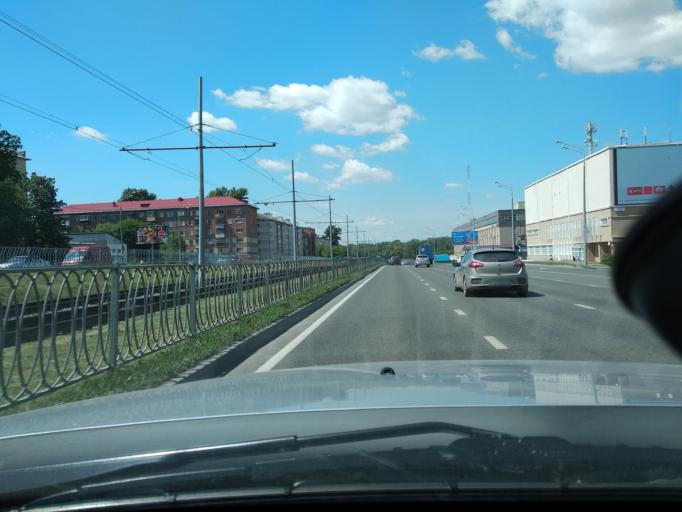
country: RU
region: Tatarstan
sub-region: Gorod Kazan'
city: Kazan
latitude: 55.8143
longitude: 49.1869
